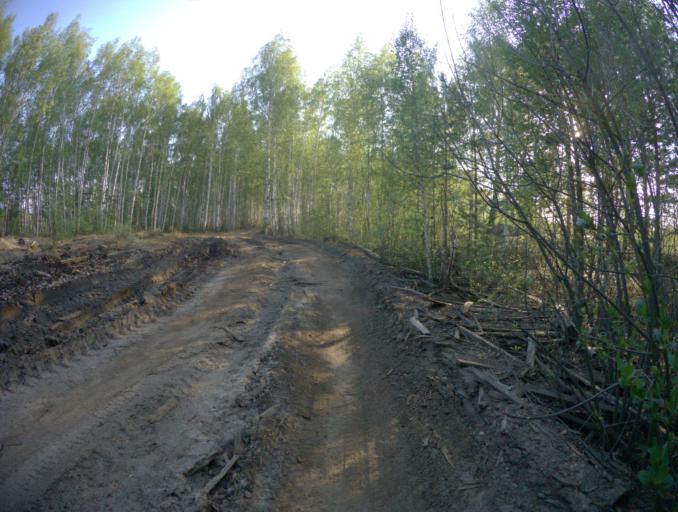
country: RU
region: Vladimir
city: Vyazniki
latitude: 56.3711
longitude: 42.1631
